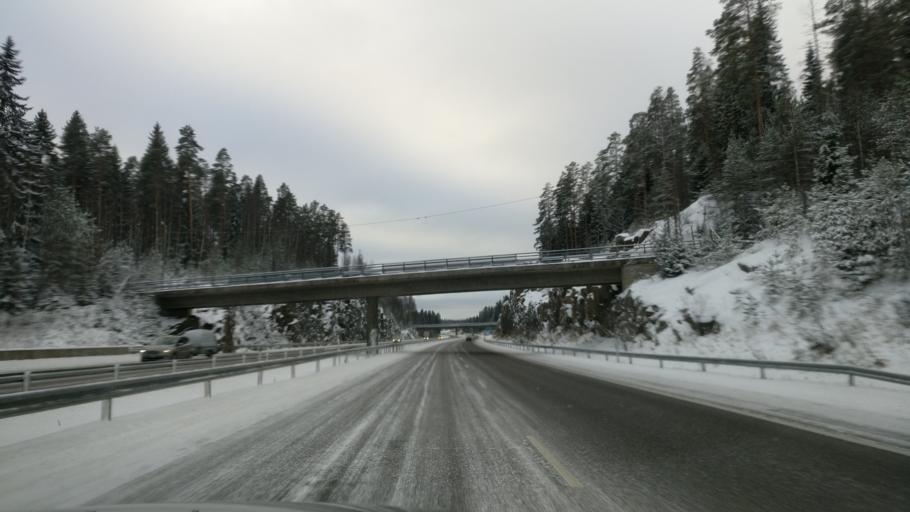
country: FI
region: Paijanne Tavastia
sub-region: Lahti
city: Nastola
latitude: 61.0054
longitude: 25.8057
